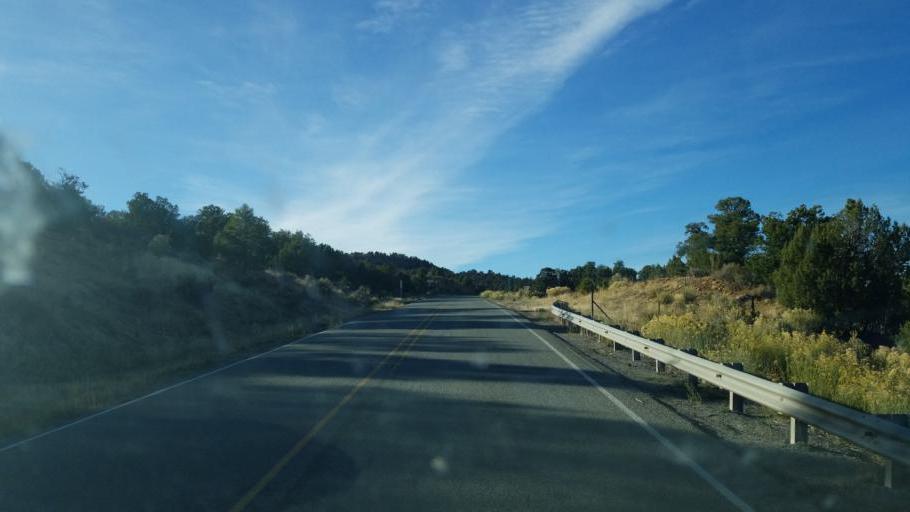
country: US
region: New Mexico
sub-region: Rio Arriba County
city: Navajo
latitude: 36.7119
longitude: -107.3223
